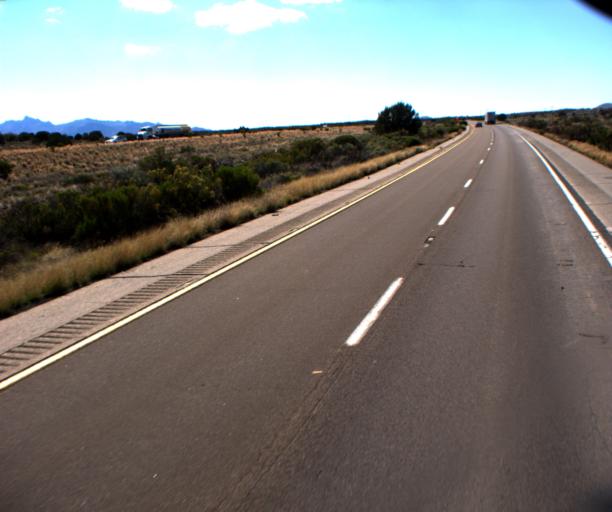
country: US
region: Arizona
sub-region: Mohave County
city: New Kingman-Butler
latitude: 35.1422
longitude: -113.6772
